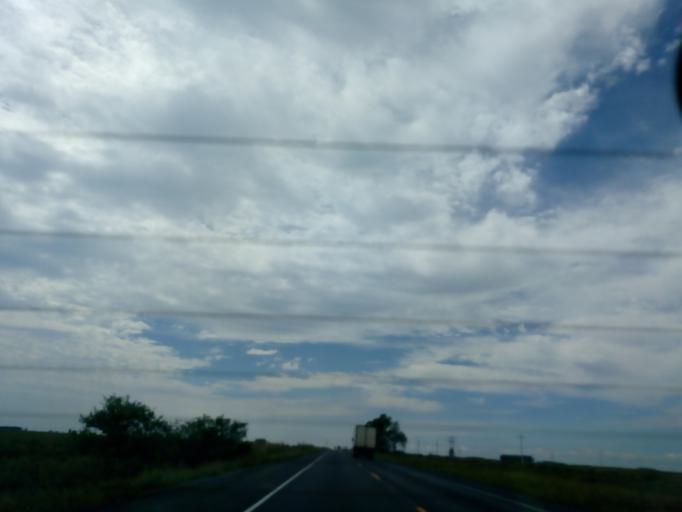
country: BR
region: Rio Grande do Sul
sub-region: Quarai
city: Quarai
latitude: -29.9784
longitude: -56.5468
